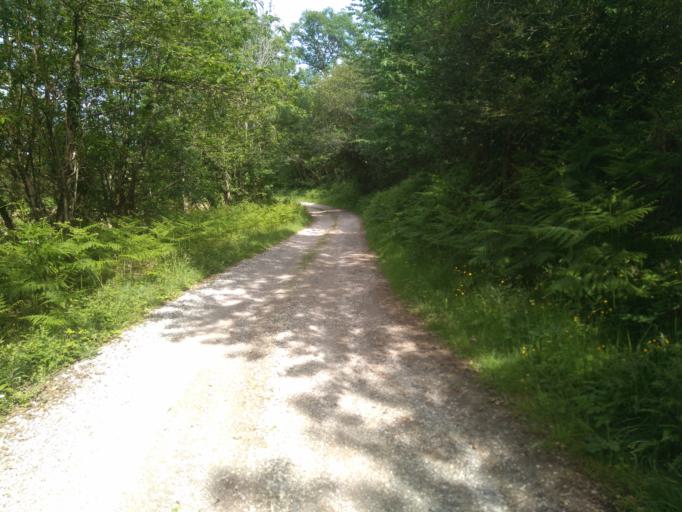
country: FR
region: Aquitaine
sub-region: Departement des Pyrenees-Atlantiques
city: Orthez
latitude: 43.4612
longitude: -0.7880
